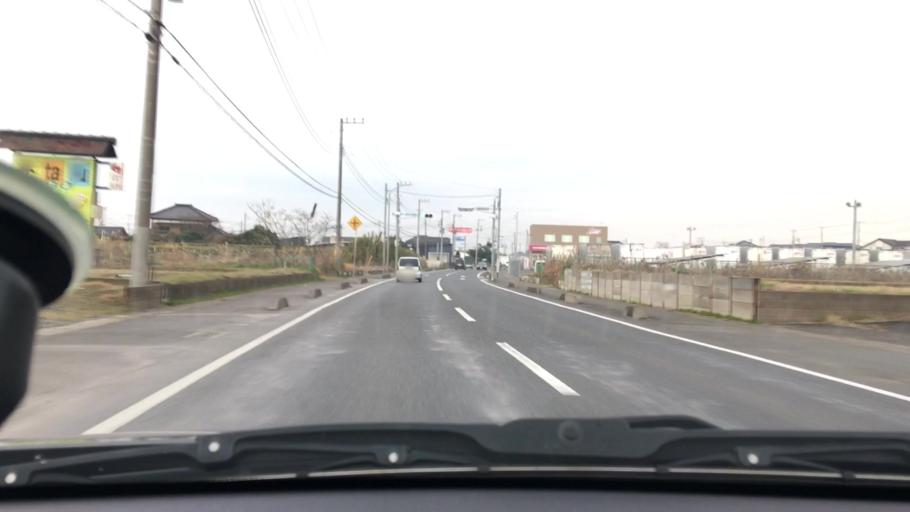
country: JP
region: Chiba
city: Omigawa
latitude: 35.8755
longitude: 140.6335
